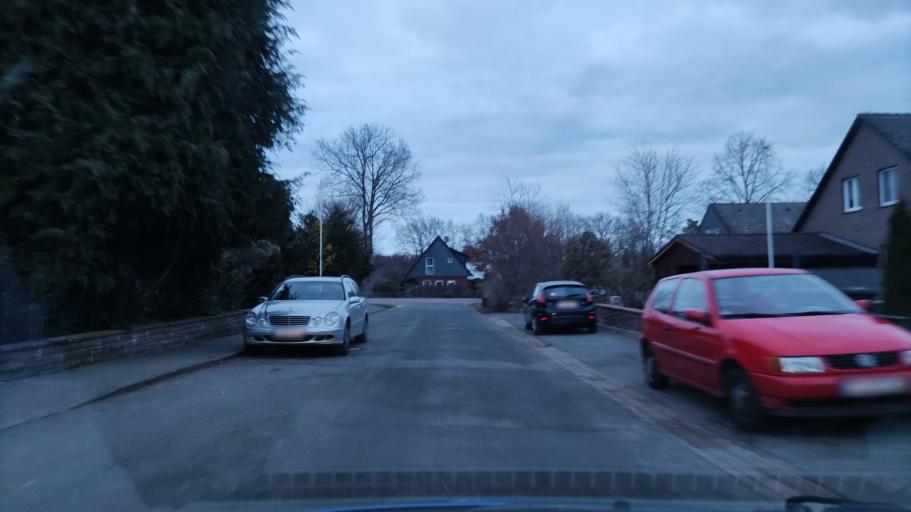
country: DE
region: Lower Saxony
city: Wendisch Evern
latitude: 53.2141
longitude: 10.4796
